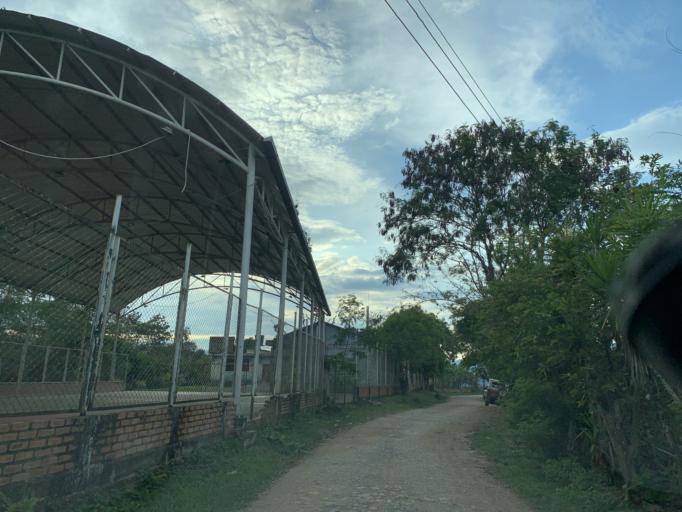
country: CO
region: Boyaca
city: Santana
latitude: 6.0823
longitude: -73.4938
